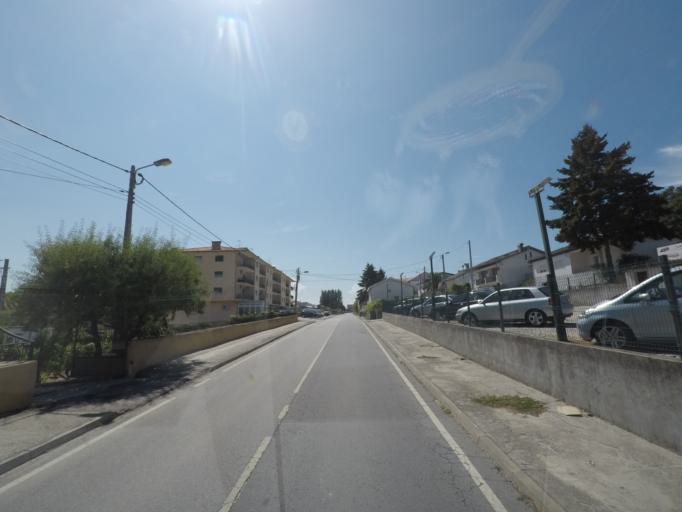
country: PT
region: Vila Real
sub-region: Sabrosa
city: Sabrosa
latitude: 41.2677
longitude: -7.4793
